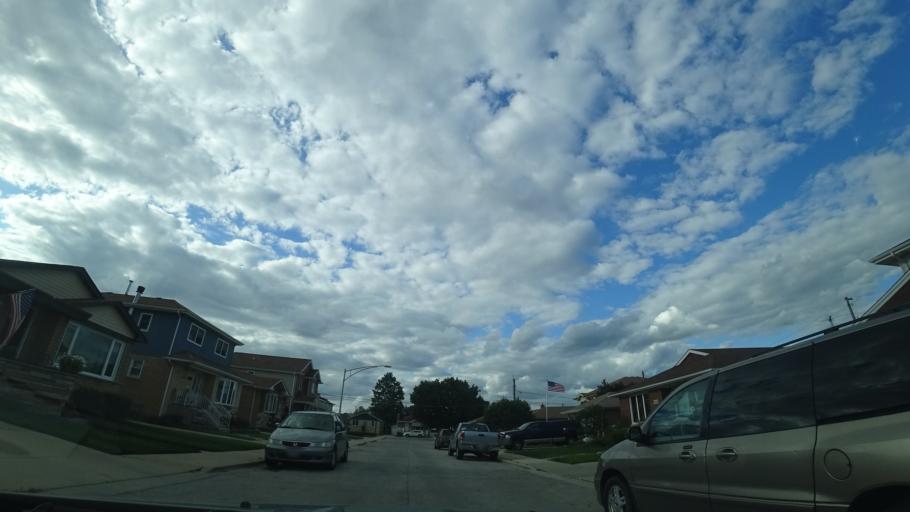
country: US
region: Illinois
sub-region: Cook County
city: Merrionette Park
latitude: 41.6868
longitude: -87.7147
